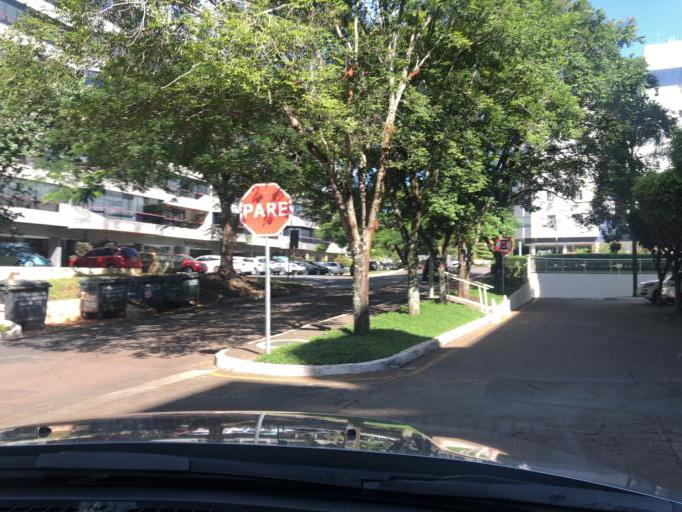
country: BR
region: Federal District
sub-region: Brasilia
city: Brasilia
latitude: -15.8009
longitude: -47.9221
